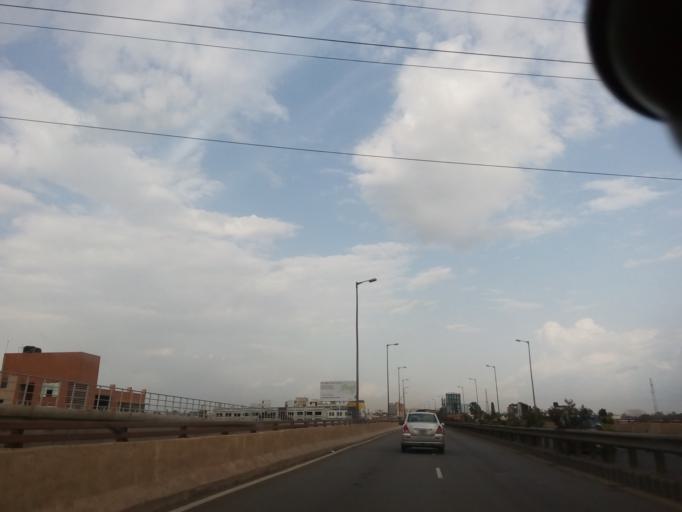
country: IN
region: Karnataka
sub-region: Bangalore Urban
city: Yelahanka
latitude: 13.0466
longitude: 77.5033
